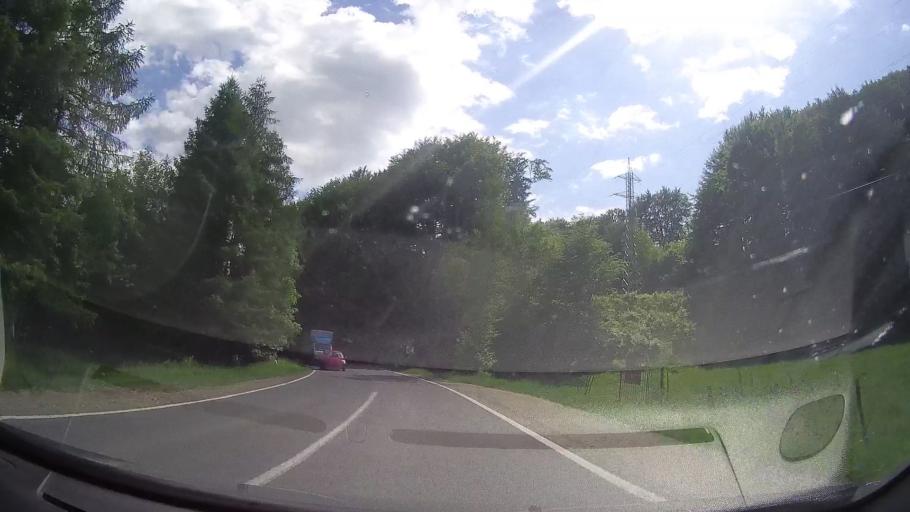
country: RO
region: Prahova
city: Maneciu
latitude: 45.4141
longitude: 25.9424
